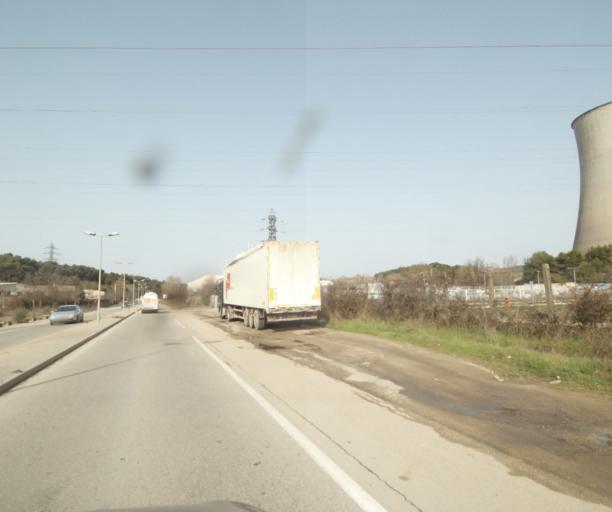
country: FR
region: Provence-Alpes-Cote d'Azur
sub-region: Departement des Bouches-du-Rhone
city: Gardanne
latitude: 43.4658
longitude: 5.4833
